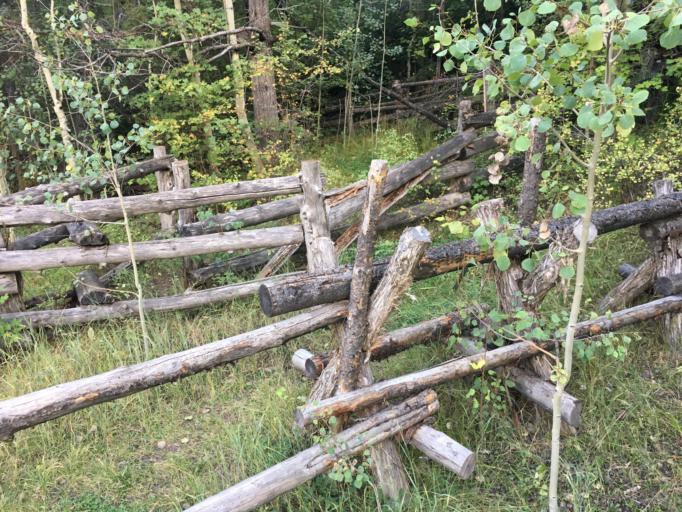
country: US
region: Utah
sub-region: Garfield County
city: Panguitch
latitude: 37.4502
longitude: -112.2410
